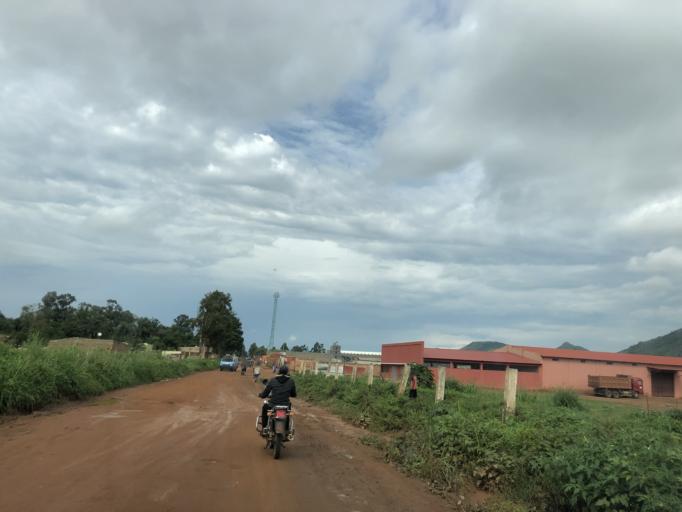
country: AO
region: Cuanza Sul
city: Uacu Cungo
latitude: -11.3478
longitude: 15.1036
